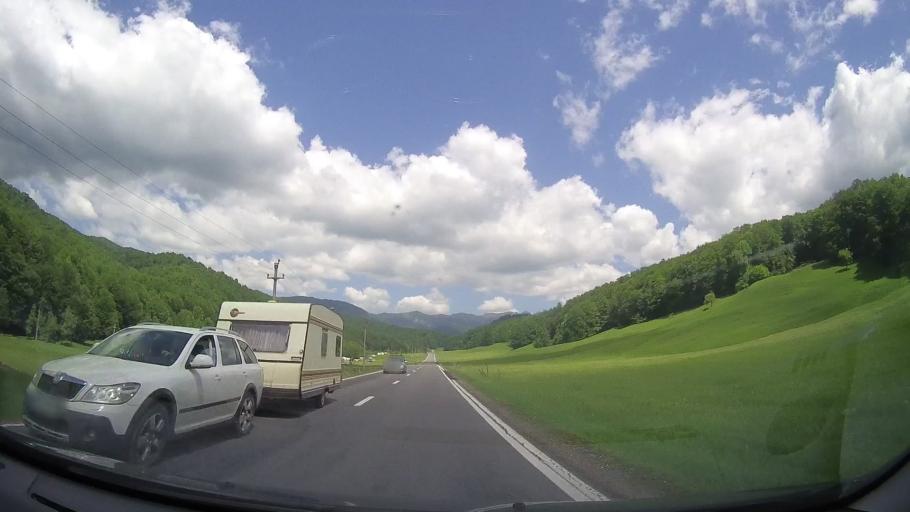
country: RO
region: Prahova
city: Maneciu
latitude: 45.4224
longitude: 25.9422
